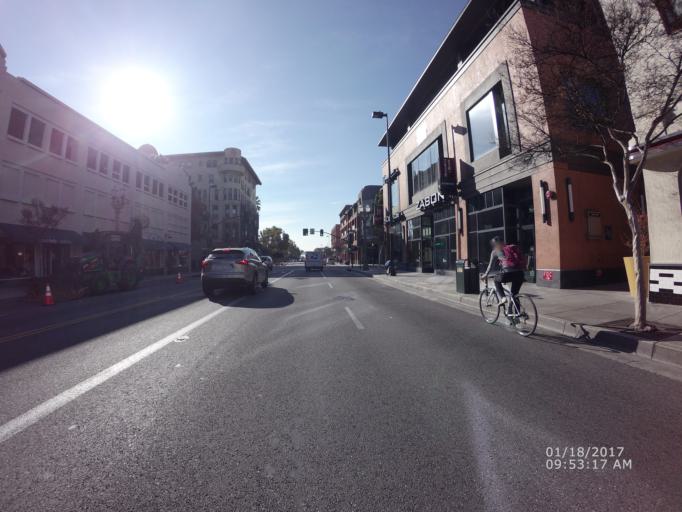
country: US
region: California
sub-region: Los Angeles County
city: Pasadena
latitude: 34.1449
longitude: -118.1505
